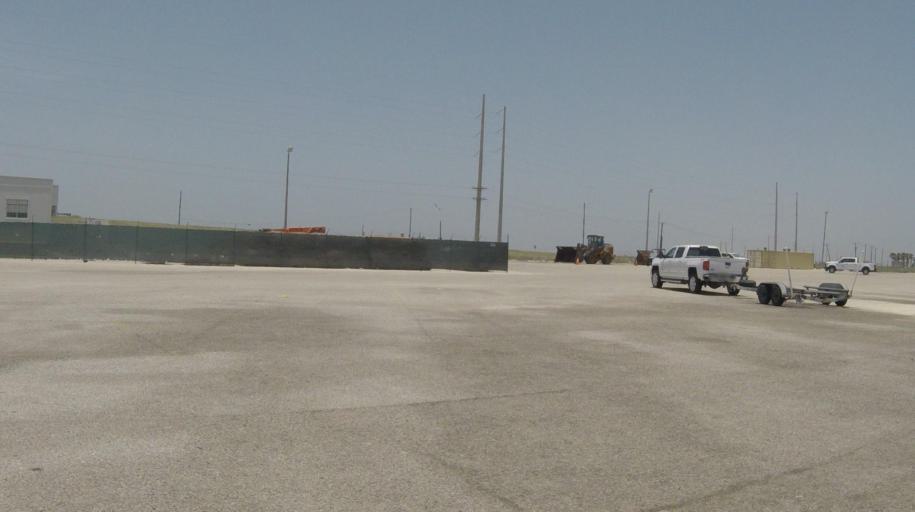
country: US
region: Texas
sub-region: Nueces County
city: Corpus Christi
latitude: 27.6186
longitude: -97.2120
